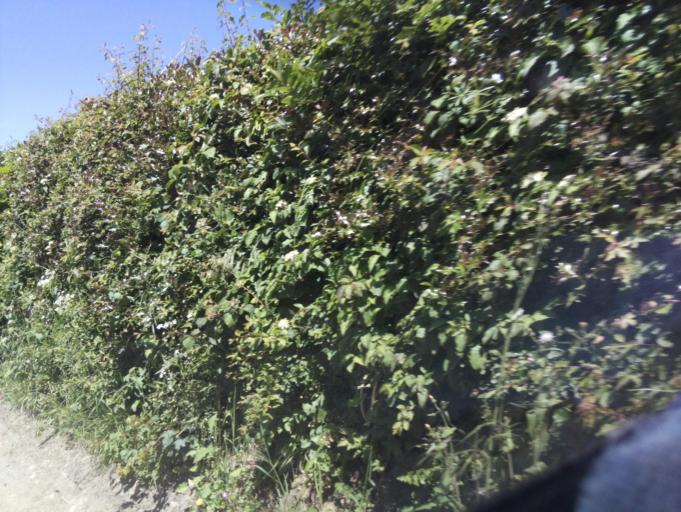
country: GB
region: Wales
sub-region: Monmouthshire
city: Rogiet
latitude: 51.5889
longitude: -2.8048
